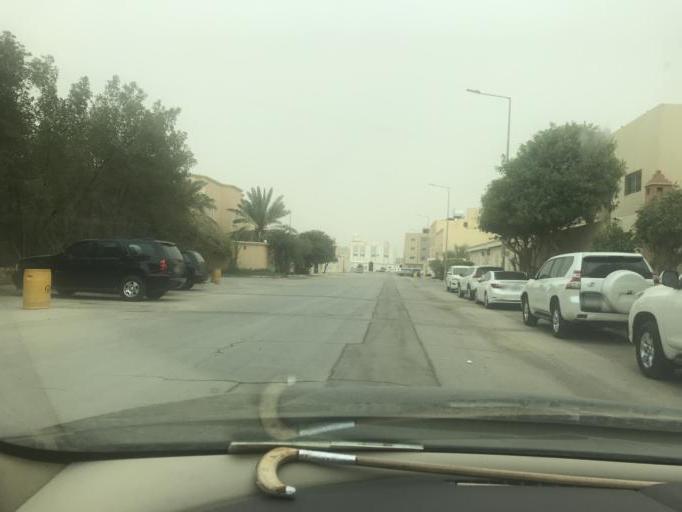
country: SA
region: Ar Riyad
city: Riyadh
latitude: 24.7275
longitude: 46.7895
